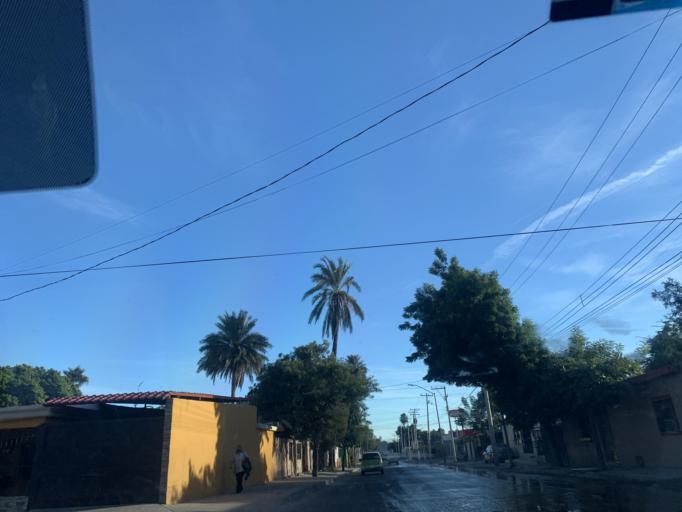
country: MX
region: Sonora
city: Hermosillo
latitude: 29.0845
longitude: -110.9267
